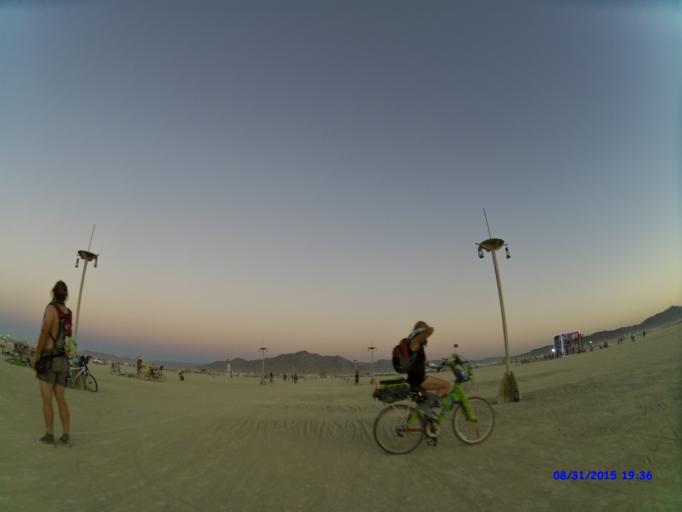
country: US
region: Nevada
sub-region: Pershing County
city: Lovelock
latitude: 40.7834
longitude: -119.2025
